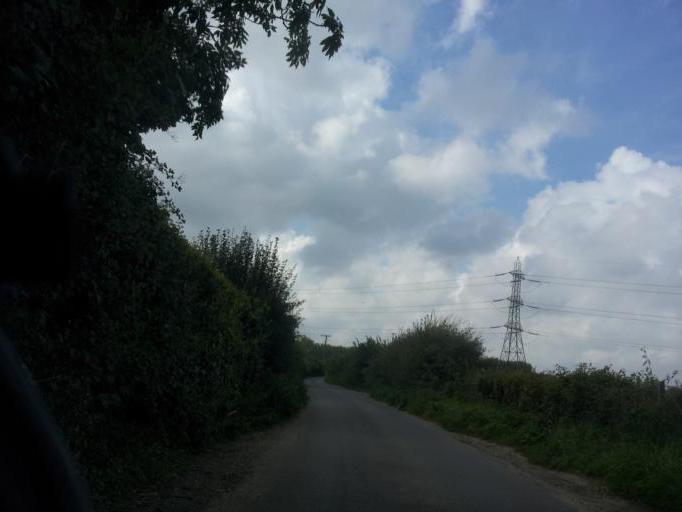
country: GB
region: England
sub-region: Kent
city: Rainham
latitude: 51.3474
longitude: 0.6309
